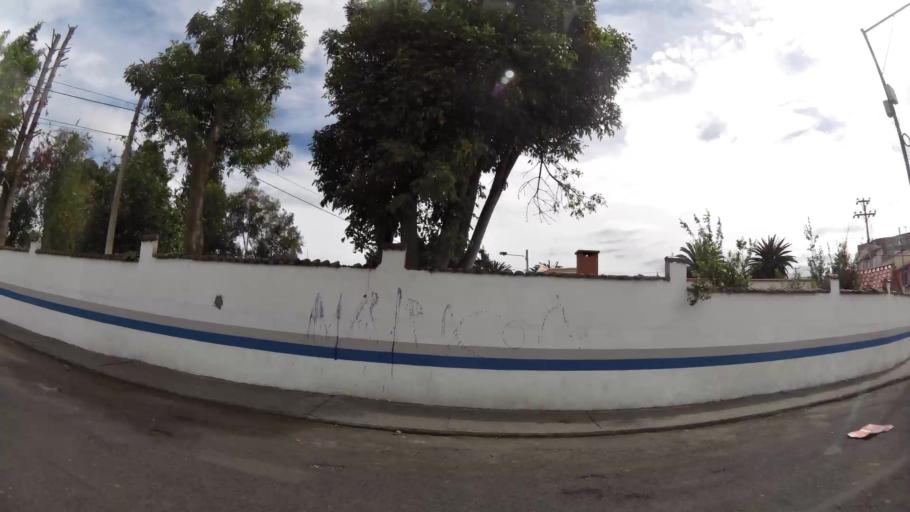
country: EC
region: Cotopaxi
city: Latacunga
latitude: -0.9257
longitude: -78.6051
